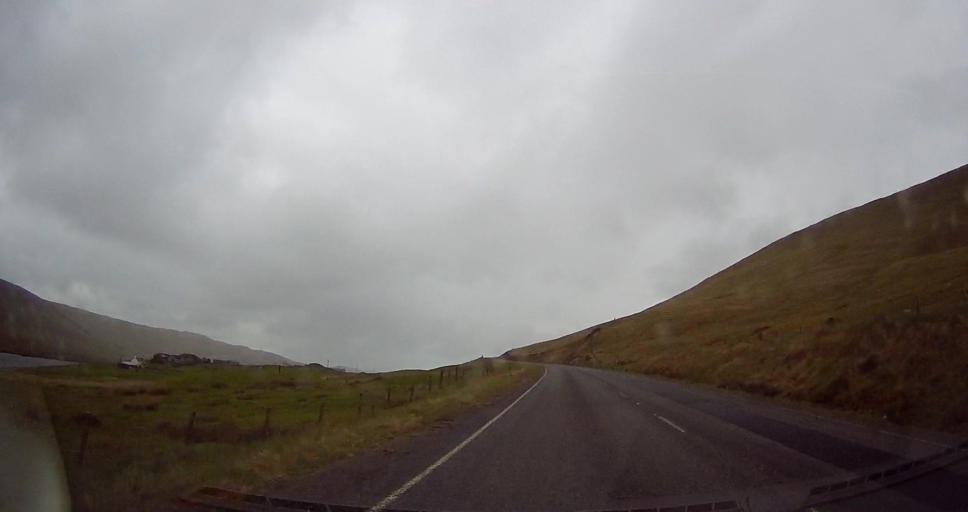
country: GB
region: Scotland
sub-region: Shetland Islands
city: Lerwick
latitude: 60.2523
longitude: -1.2993
